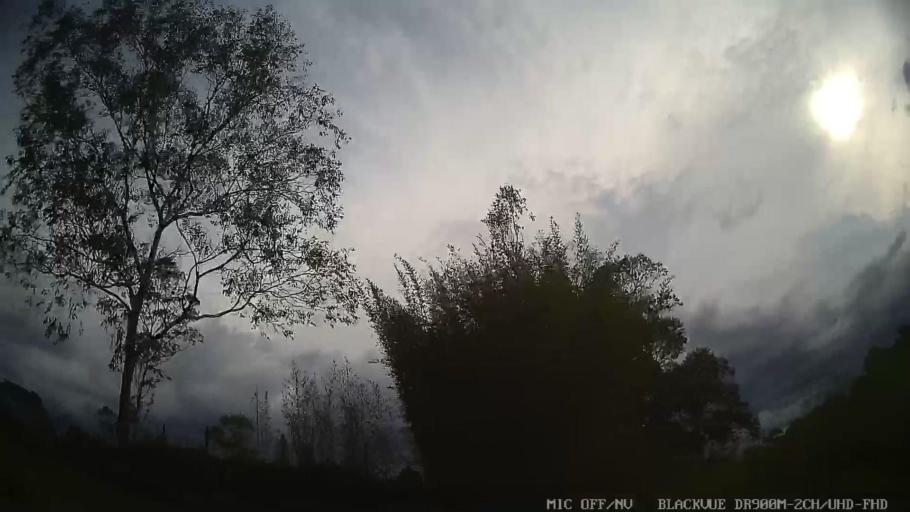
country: BR
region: Sao Paulo
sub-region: Amparo
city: Amparo
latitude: -22.7629
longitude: -46.7560
